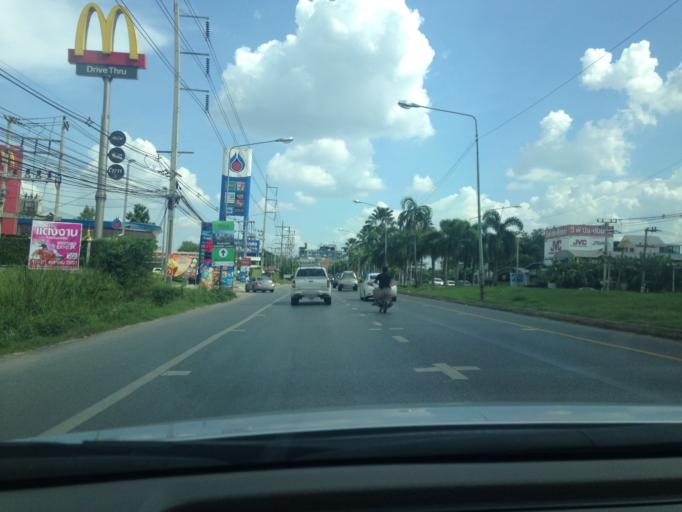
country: TH
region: Phra Nakhon Si Ayutthaya
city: Ban Bang Kadi Pathum Thani
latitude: 13.9866
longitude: 100.5870
